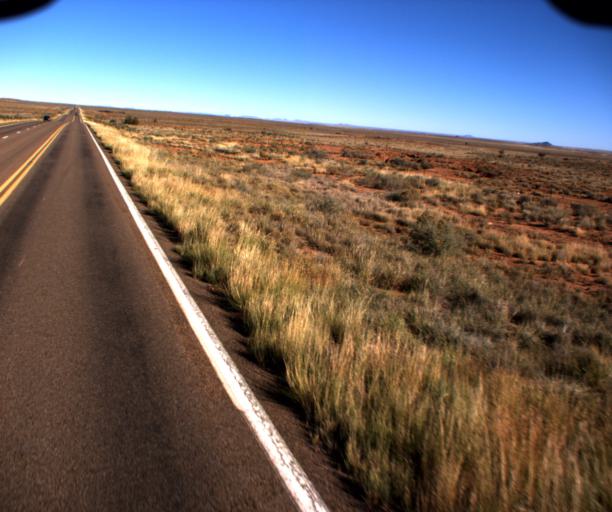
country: US
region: Arizona
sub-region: Navajo County
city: Snowflake
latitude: 34.7022
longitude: -110.1091
